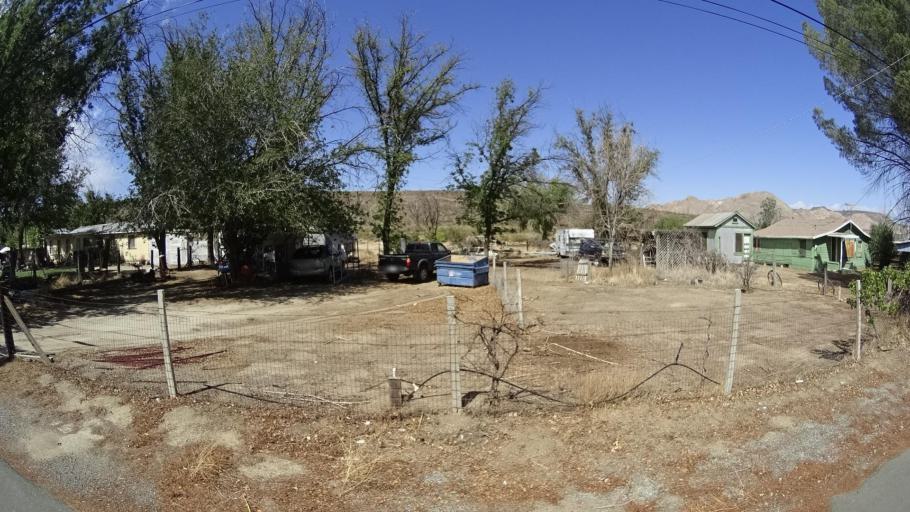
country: MX
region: Baja California
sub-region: Tecate
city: Cereso del Hongo
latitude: 32.6211
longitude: -116.1854
